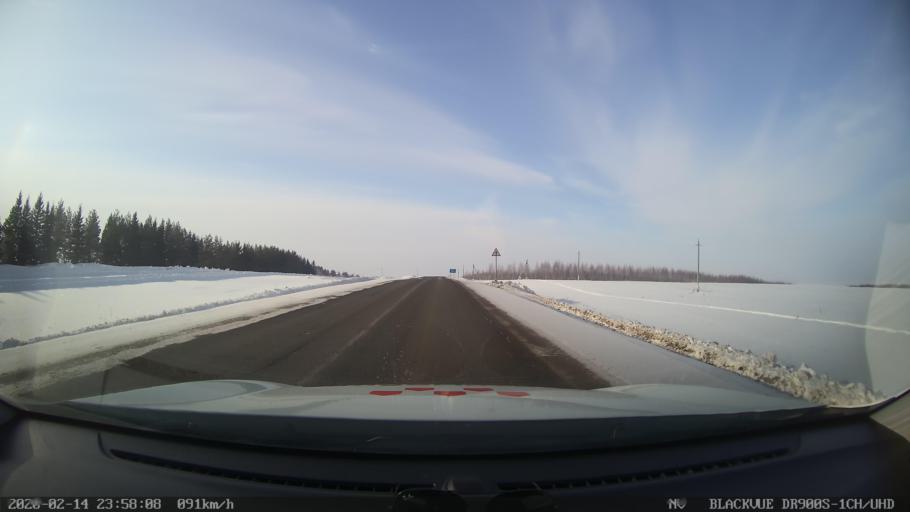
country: RU
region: Tatarstan
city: Kuybyshevskiy Zaton
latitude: 55.3388
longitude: 49.0943
